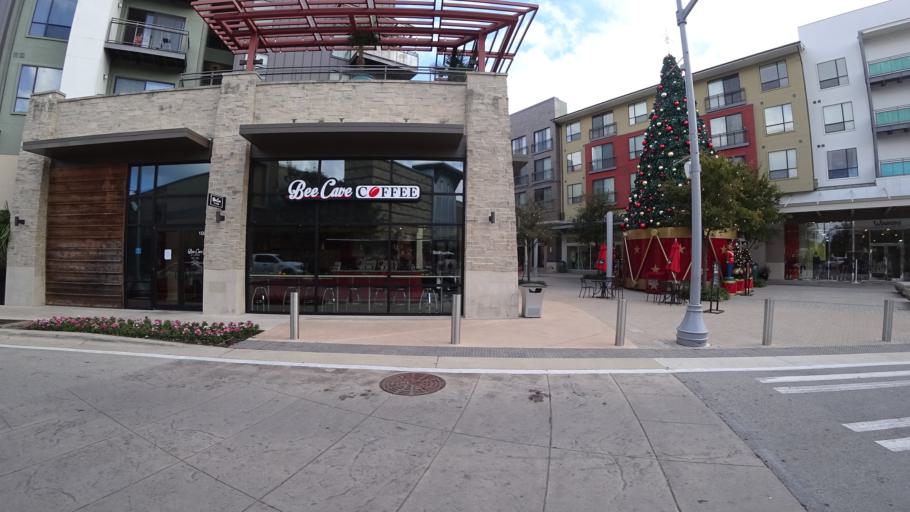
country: US
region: Texas
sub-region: Williamson County
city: Jollyville
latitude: 30.3965
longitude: -97.7274
